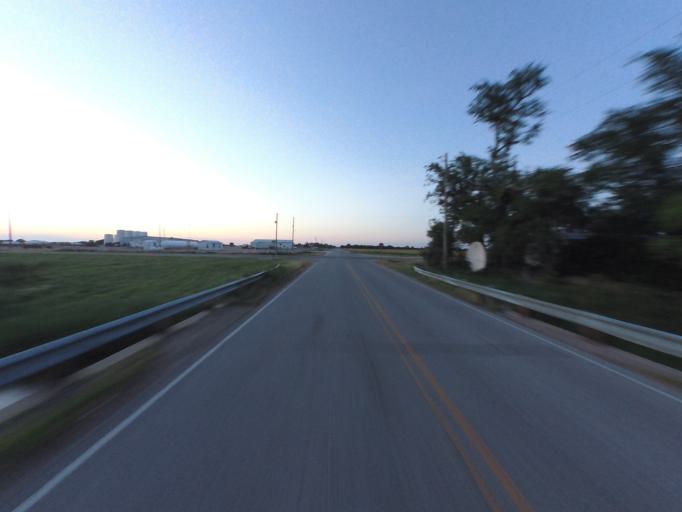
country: US
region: Kansas
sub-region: Reno County
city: Nickerson
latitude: 38.0571
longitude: -98.0875
